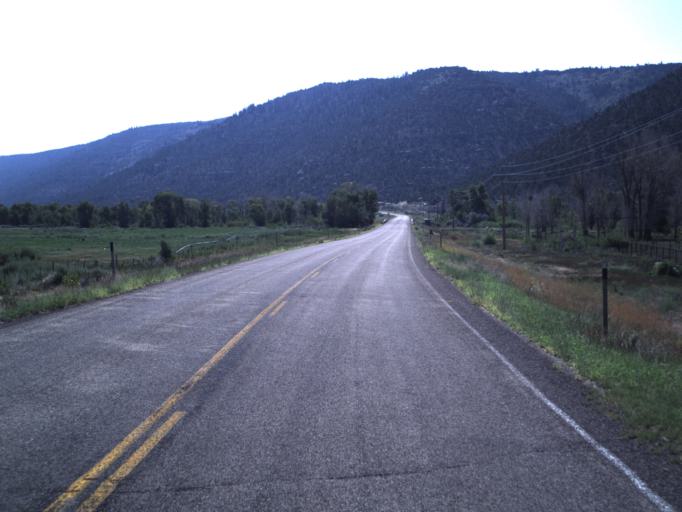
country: US
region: Utah
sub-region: Duchesne County
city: Duchesne
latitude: 40.3015
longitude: -110.6068
